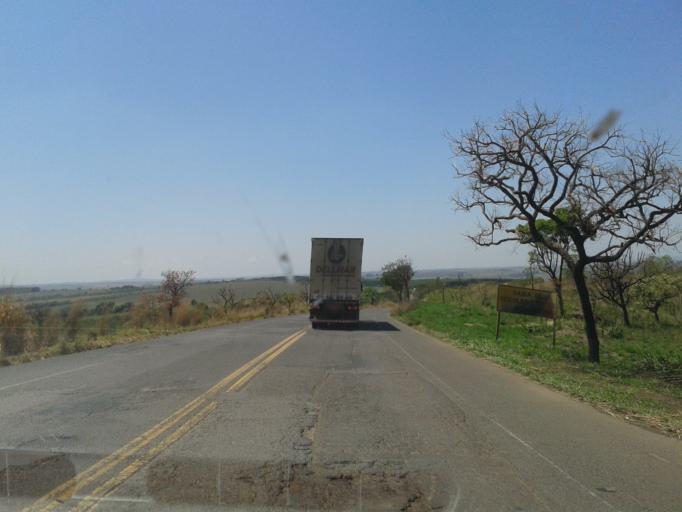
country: BR
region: Minas Gerais
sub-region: Araxa
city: Araxa
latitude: -19.4300
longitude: -47.2273
